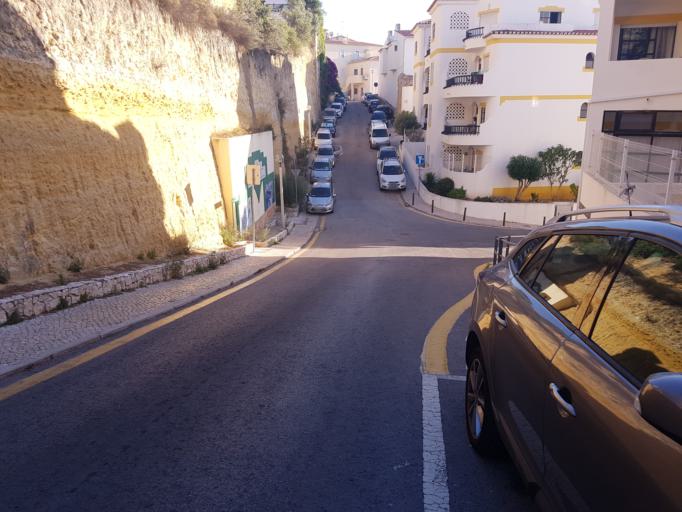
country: PT
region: Faro
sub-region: Lagoa
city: Carvoeiro
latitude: 37.0985
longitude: -8.4696
